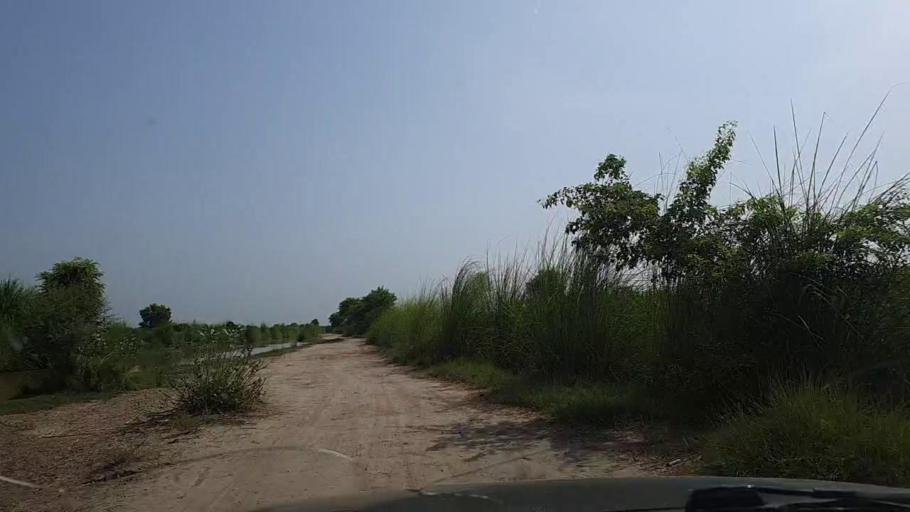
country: PK
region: Sindh
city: Ghotki
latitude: 28.0605
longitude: 69.3811
